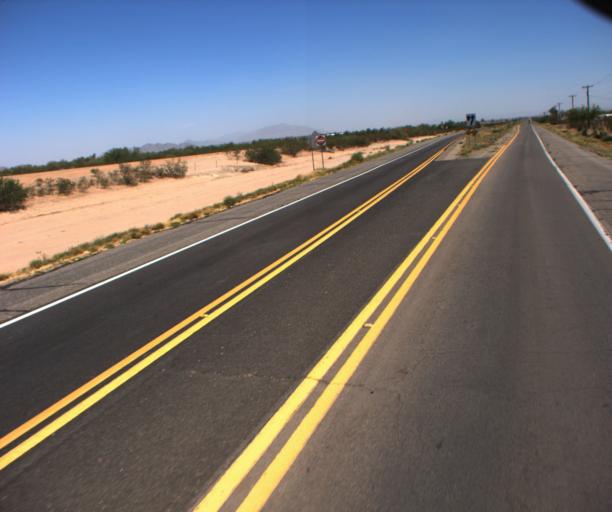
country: US
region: Arizona
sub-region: Pinal County
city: Maricopa
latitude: 32.8817
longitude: -112.0493
